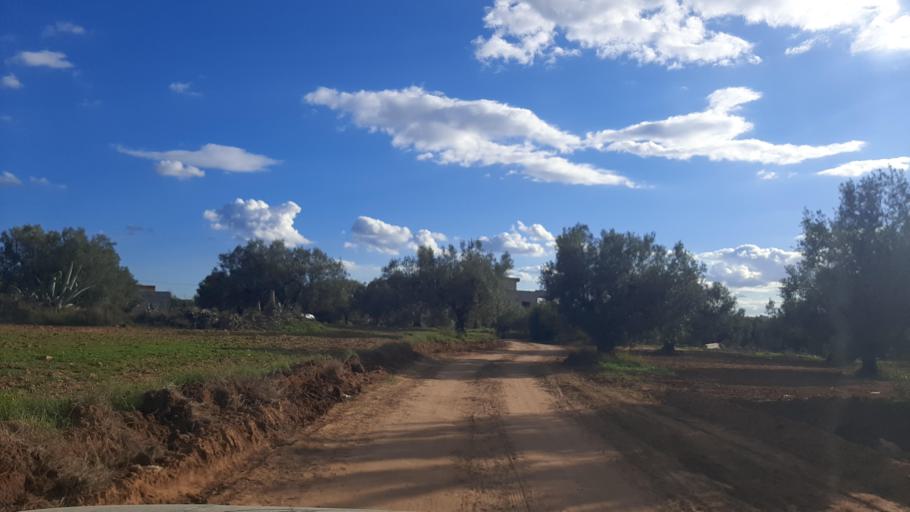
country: TN
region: Nabul
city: Al Hammamat
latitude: 36.4286
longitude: 10.5064
